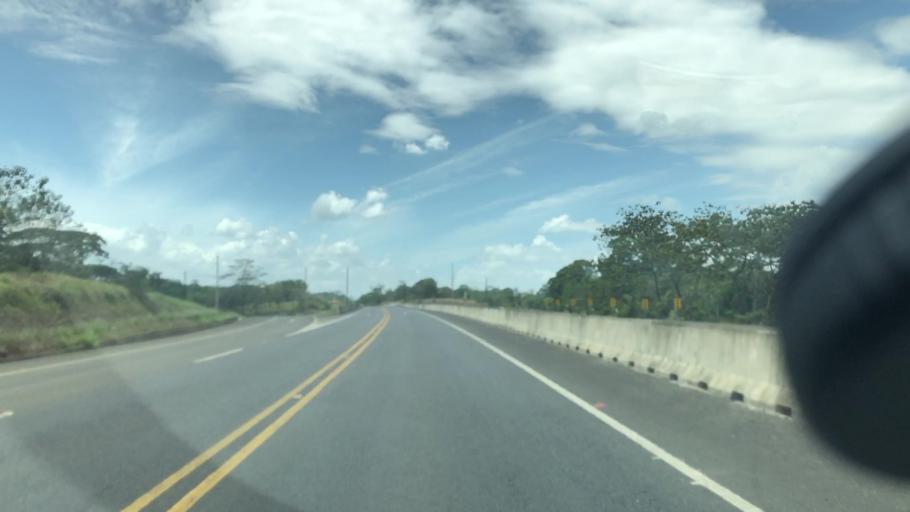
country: CR
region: Heredia
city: La Virgen
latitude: 10.4407
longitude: -84.1575
